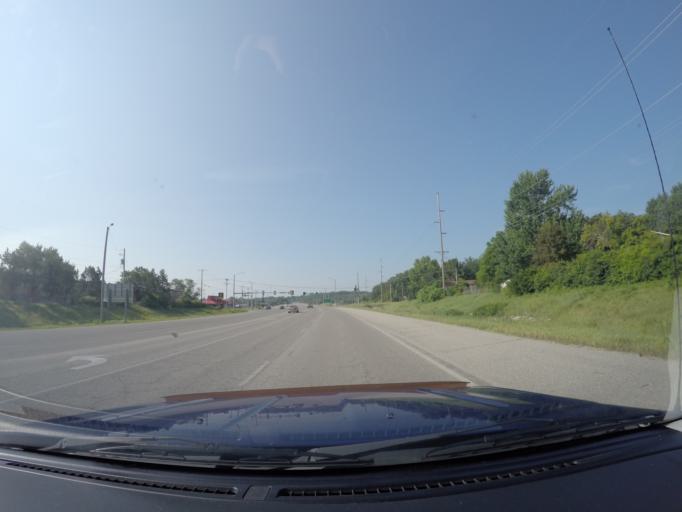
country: US
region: Kansas
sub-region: Riley County
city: Manhattan
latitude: 39.1940
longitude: -96.6125
